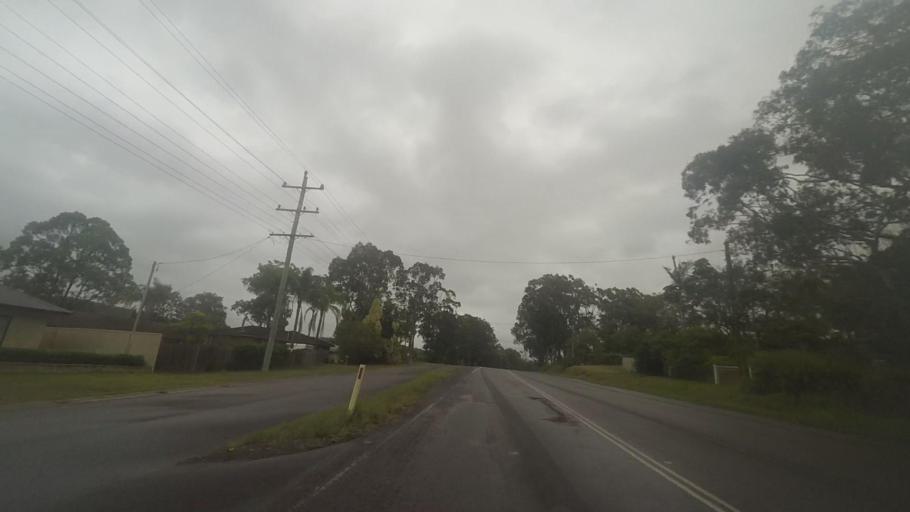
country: AU
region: New South Wales
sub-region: Port Stephens Shire
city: Medowie
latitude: -32.6536
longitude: 151.9555
